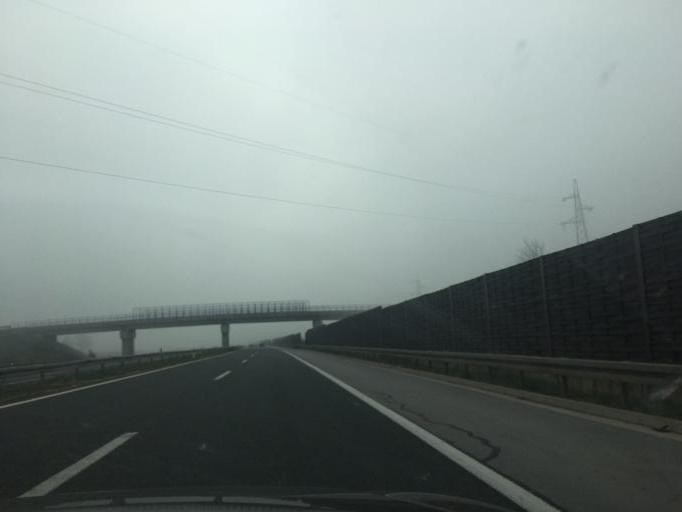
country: HR
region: Licko-Senjska
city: Gospic
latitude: 44.5276
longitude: 15.4519
